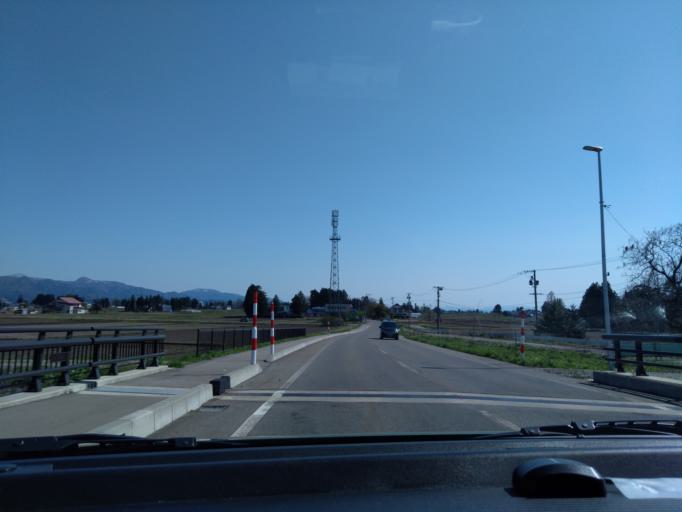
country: JP
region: Akita
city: Kakunodatemachi
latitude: 39.5431
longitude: 140.5856
